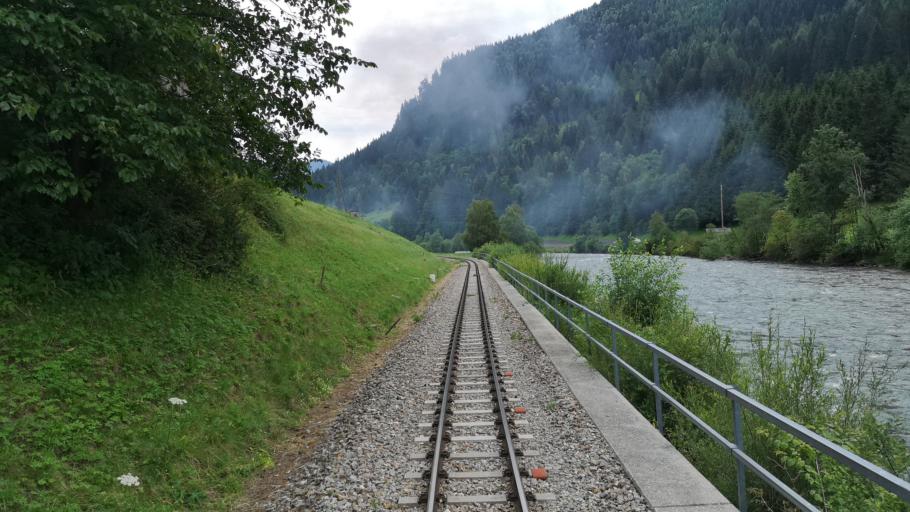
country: AT
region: Salzburg
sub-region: Politischer Bezirk Tamsweg
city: Ramingstein
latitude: 47.0756
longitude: 13.8514
